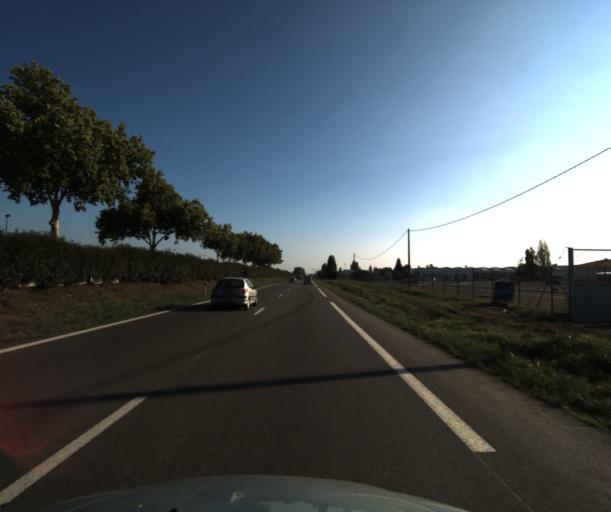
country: FR
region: Midi-Pyrenees
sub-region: Departement de la Haute-Garonne
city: Saubens
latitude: 43.4896
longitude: 1.3417
